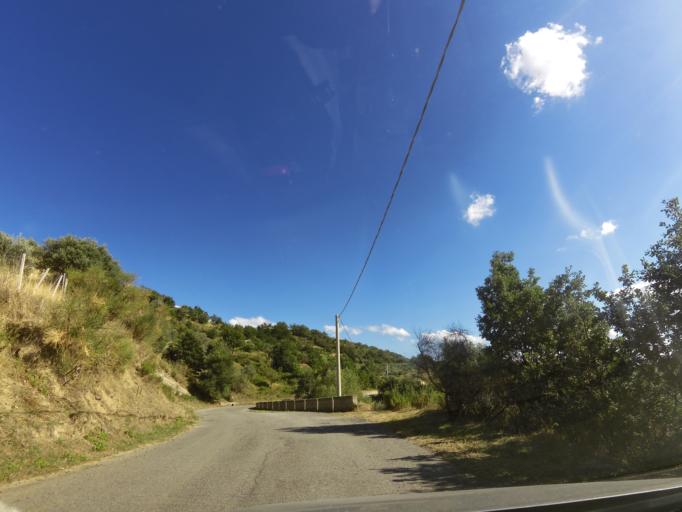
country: IT
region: Calabria
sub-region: Provincia di Reggio Calabria
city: Pazzano
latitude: 38.4522
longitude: 16.4510
